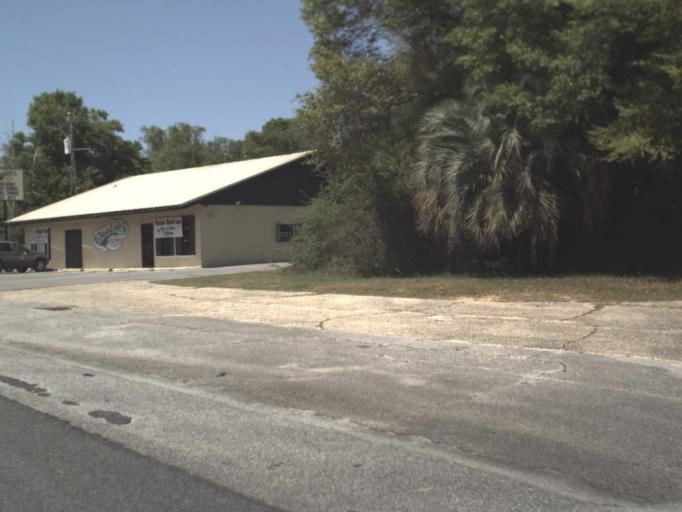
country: US
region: Florida
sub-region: Escambia County
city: Bellview
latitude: 30.4507
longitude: -87.2927
